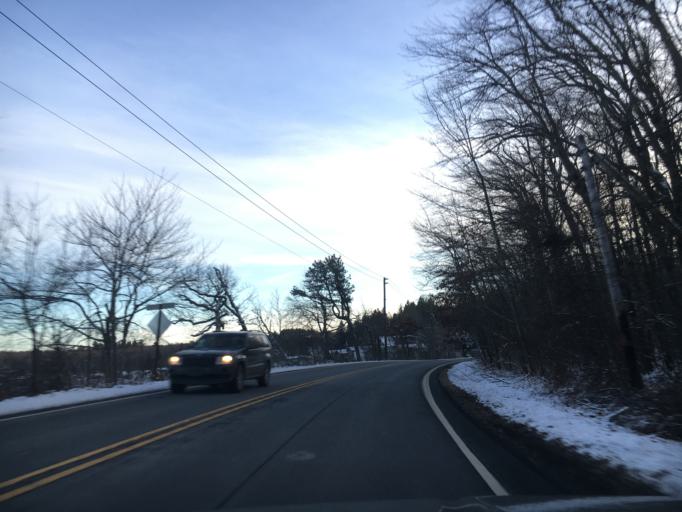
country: US
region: Pennsylvania
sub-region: Pike County
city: Hemlock Farms
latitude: 41.2512
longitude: -75.0691
